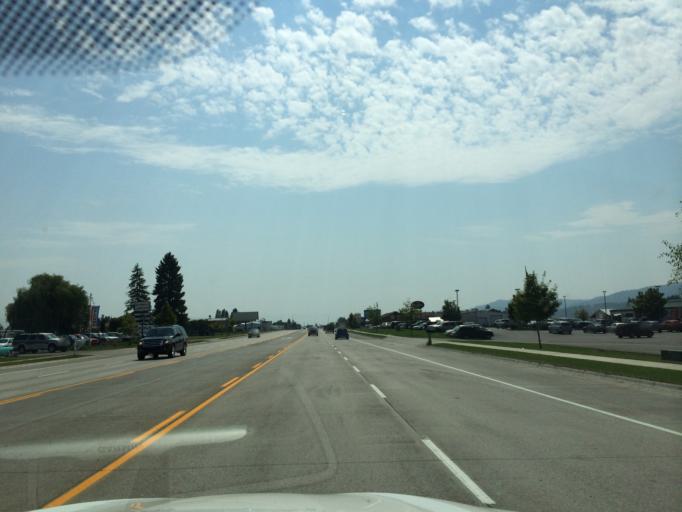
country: US
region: Montana
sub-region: Flathead County
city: Kalispell
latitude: 48.1756
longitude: -114.2987
